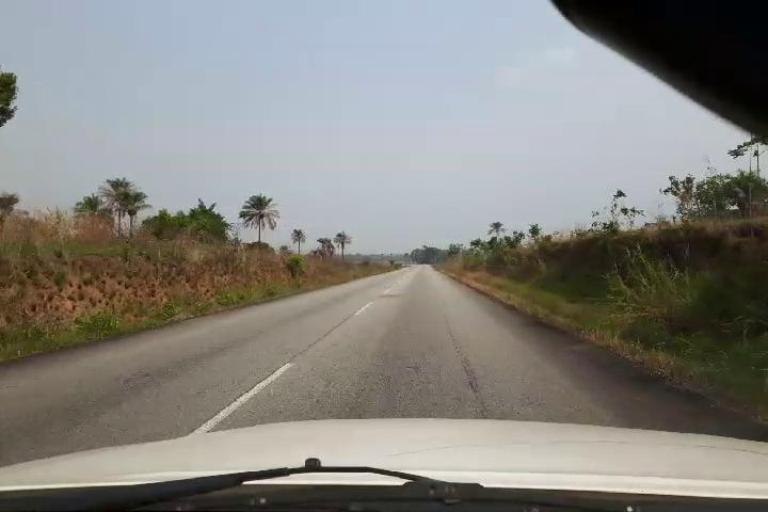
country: SL
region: Southern Province
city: Baiima
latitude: 8.1499
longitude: -11.9089
